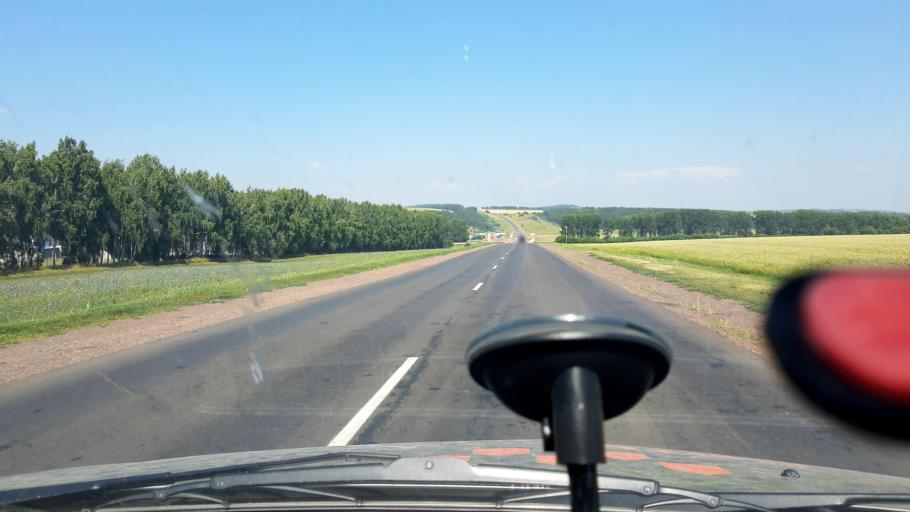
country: RU
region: Bashkortostan
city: Chekmagush
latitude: 55.1257
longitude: 54.6769
